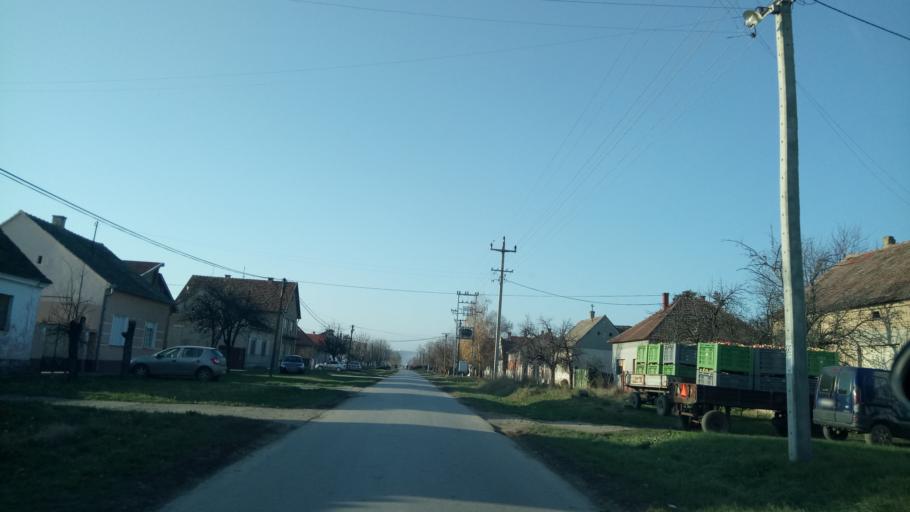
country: RS
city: Novi Slankamen
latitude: 45.1298
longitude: 20.2373
